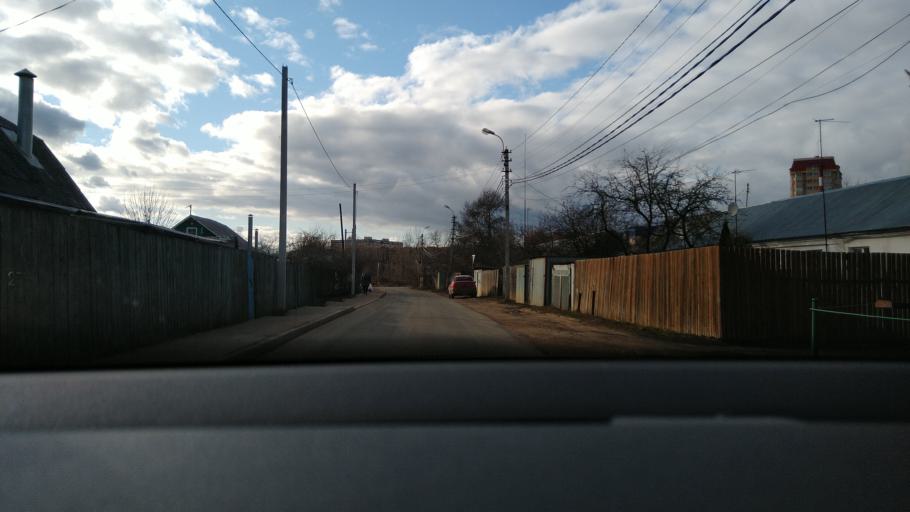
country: RU
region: Moskovskaya
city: Nakhabino
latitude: 55.8459
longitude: 37.1870
